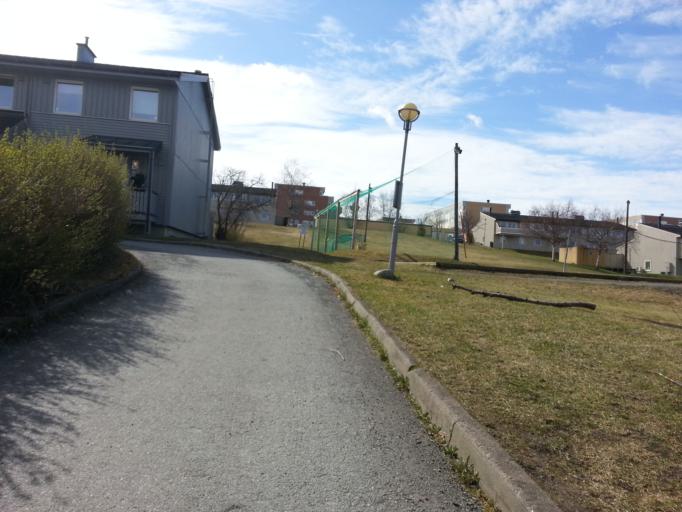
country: NO
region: Sor-Trondelag
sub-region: Trondheim
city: Trondheim
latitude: 63.4284
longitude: 10.4495
